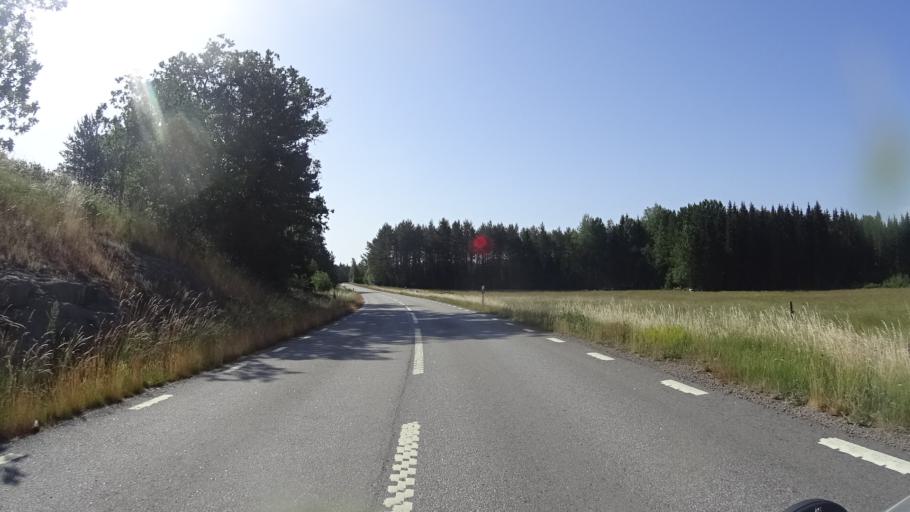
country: SE
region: OEstergoetland
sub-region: Atvidabergs Kommun
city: Atvidaberg
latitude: 58.1121
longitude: 16.1010
